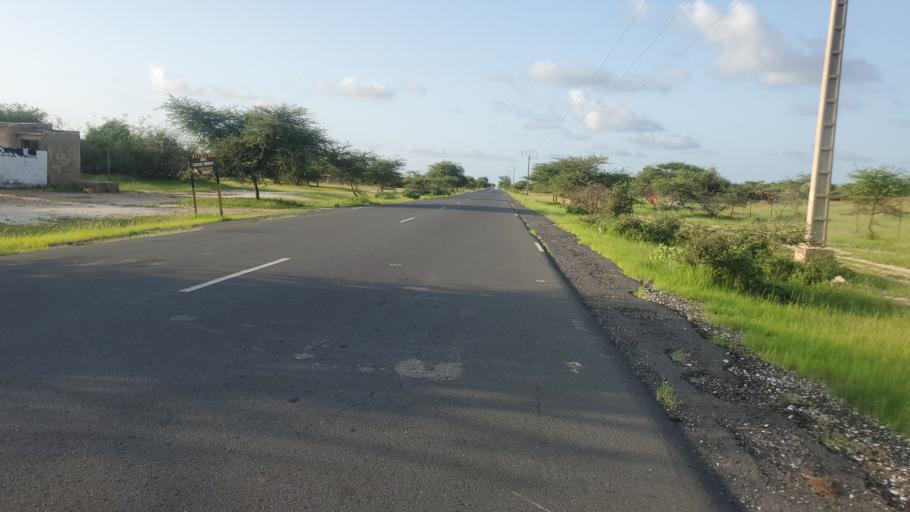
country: SN
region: Saint-Louis
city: Saint-Louis
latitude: 16.1687
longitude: -16.4098
